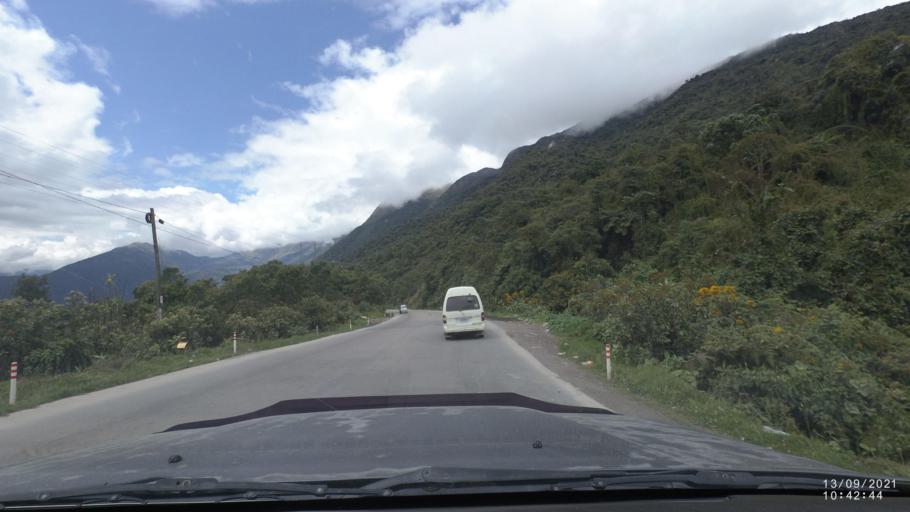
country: BO
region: Cochabamba
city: Colomi
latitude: -17.1777
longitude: -65.8879
